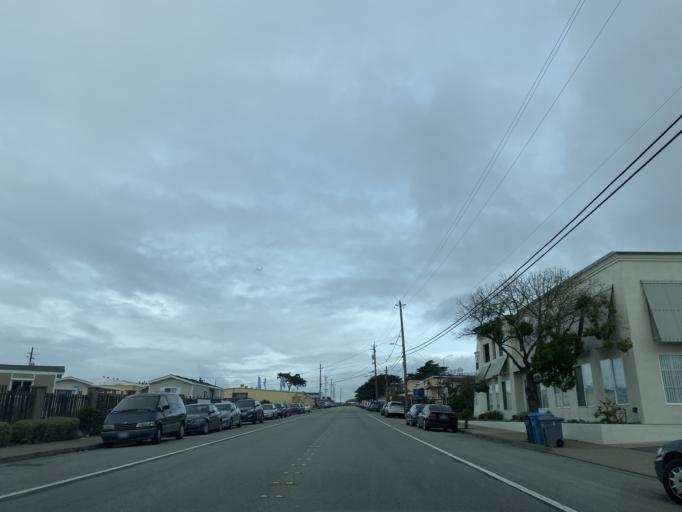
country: US
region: California
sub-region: San Mateo County
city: Pacifica
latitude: 37.6416
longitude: -122.4926
